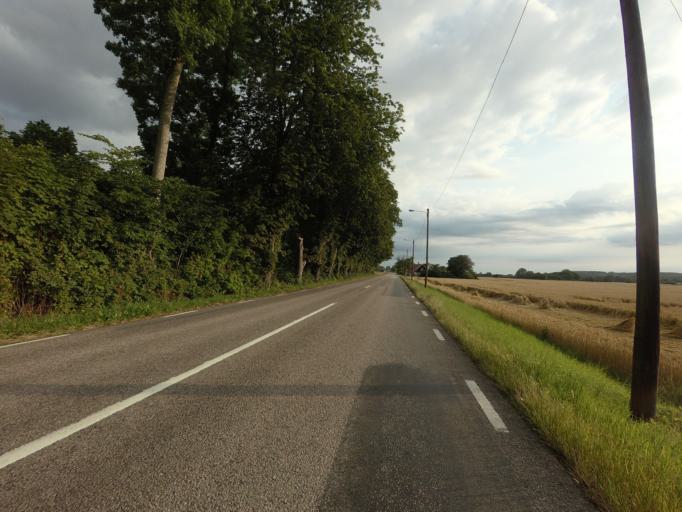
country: SE
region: Skane
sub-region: Helsingborg
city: Odakra
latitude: 56.1508
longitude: 12.6784
